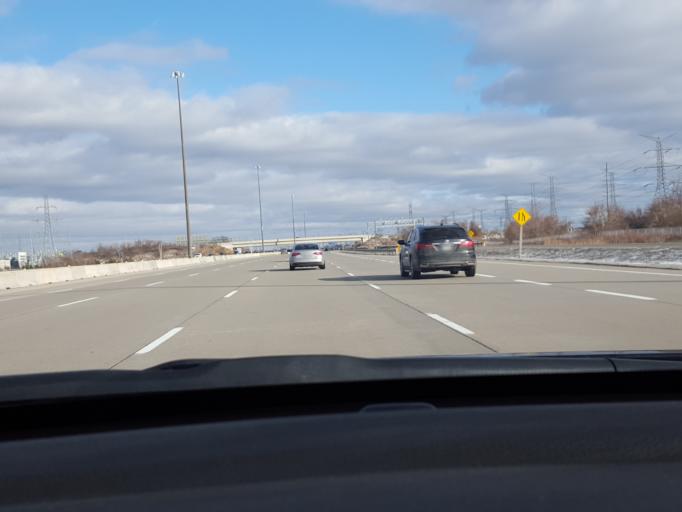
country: CA
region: Ontario
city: Willowdale
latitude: 43.8413
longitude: -79.3526
